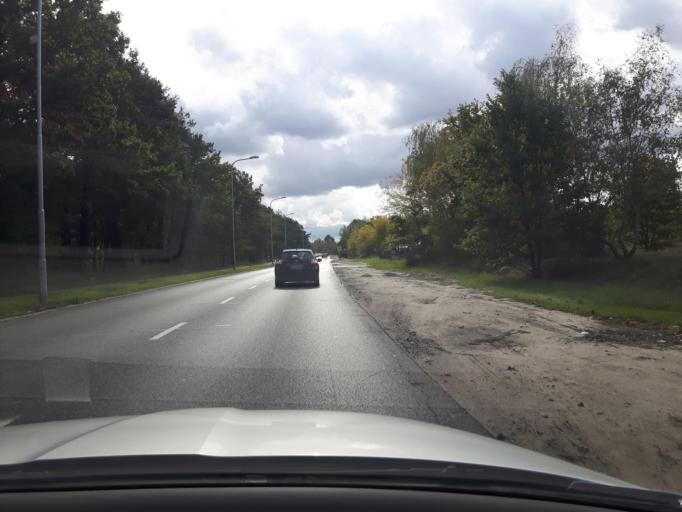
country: PL
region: Masovian Voivodeship
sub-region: Warszawa
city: Rembertow
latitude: 52.2339
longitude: 21.1437
